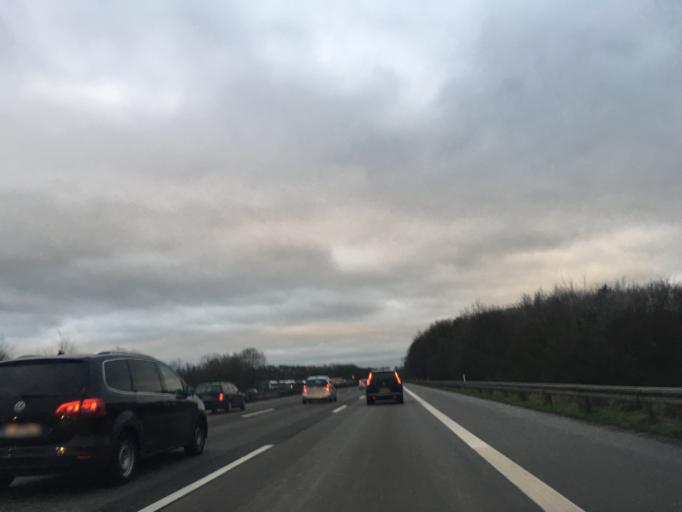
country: DE
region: North Rhine-Westphalia
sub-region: Regierungsbezirk Dusseldorf
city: Ratingen
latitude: 51.3287
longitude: 6.8866
